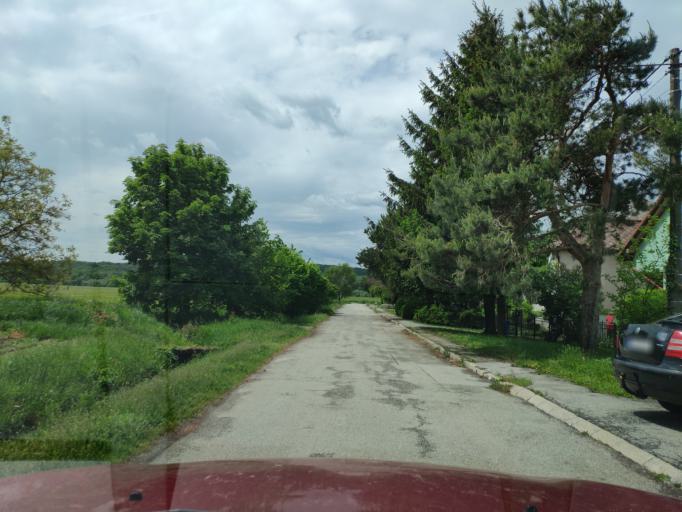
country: SK
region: Kosicky
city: Kosice
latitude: 48.7258
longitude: 21.3416
